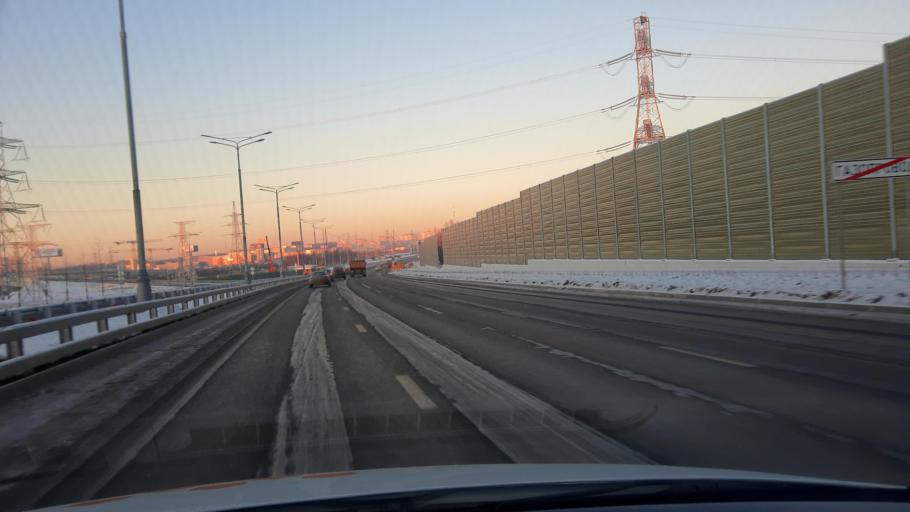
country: RU
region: Moskovskaya
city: Kommunarka
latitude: 55.5918
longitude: 37.4819
